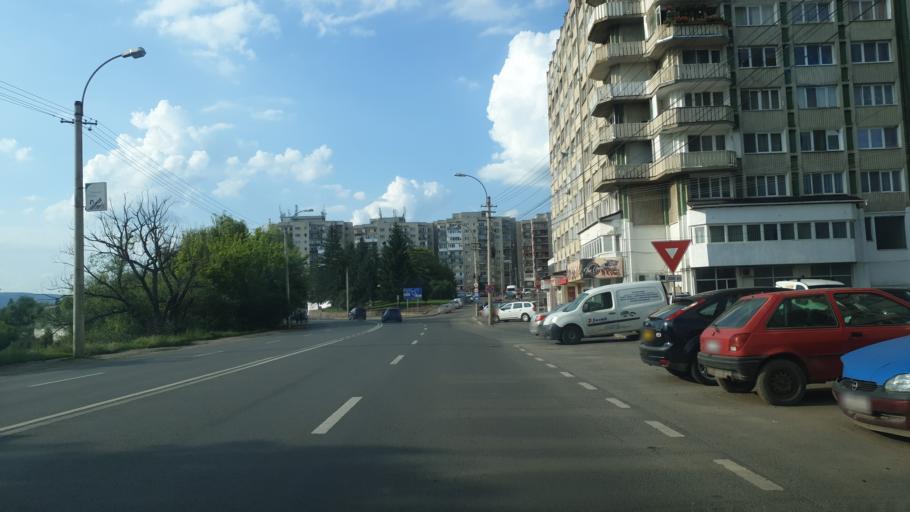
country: RO
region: Covasna
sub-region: Municipiul Sfantu Gheorghe
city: Sfantu-Gheorghe
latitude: 45.8610
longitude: 25.8077
